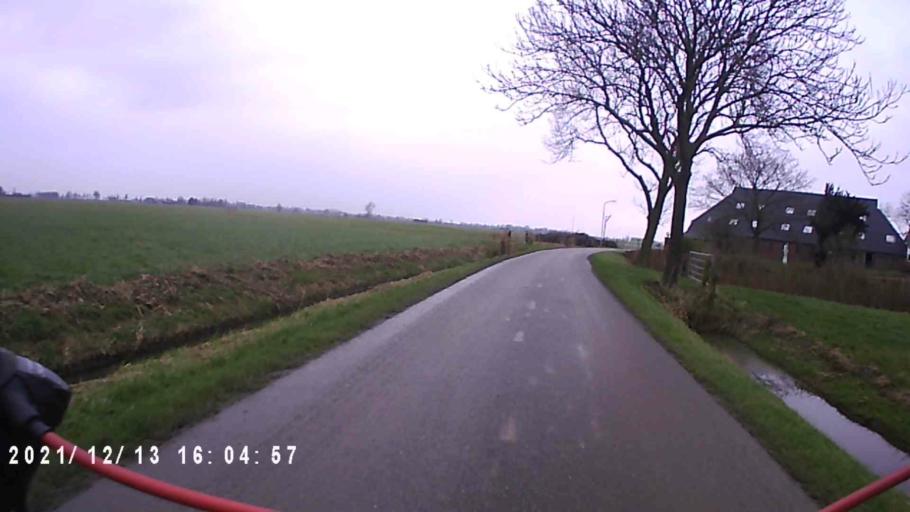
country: NL
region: Groningen
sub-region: Gemeente Appingedam
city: Appingedam
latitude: 53.3402
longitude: 6.8736
